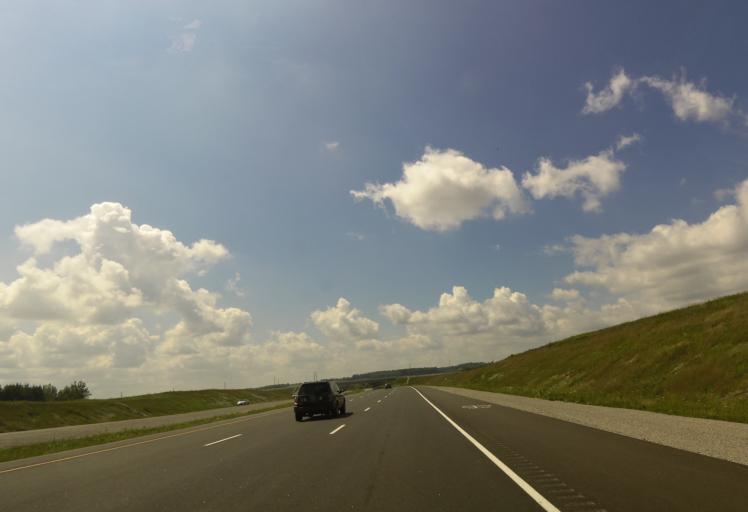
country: CA
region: Ontario
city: Pickering
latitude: 43.9398
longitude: -79.0642
